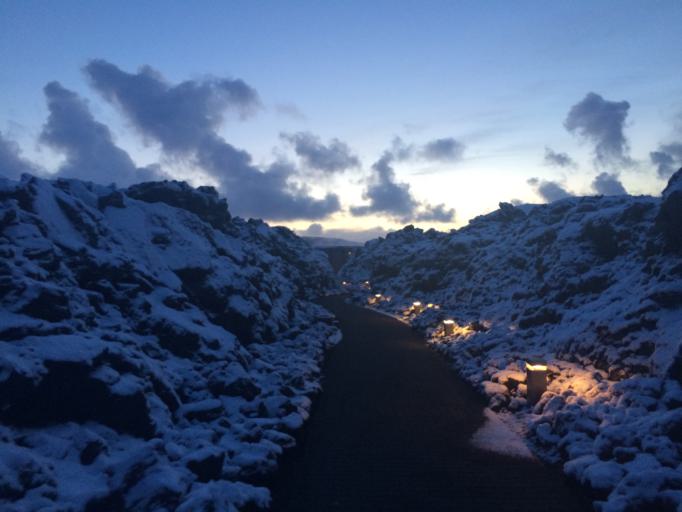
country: IS
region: Southern Peninsula
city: Grindavik
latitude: 63.8810
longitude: -22.4509
